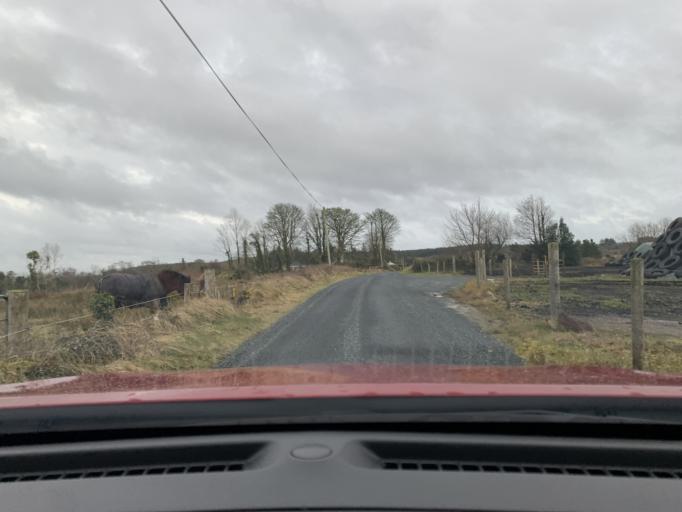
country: IE
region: Connaught
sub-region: Roscommon
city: Ballaghaderreen
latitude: 53.9687
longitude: -8.5191
